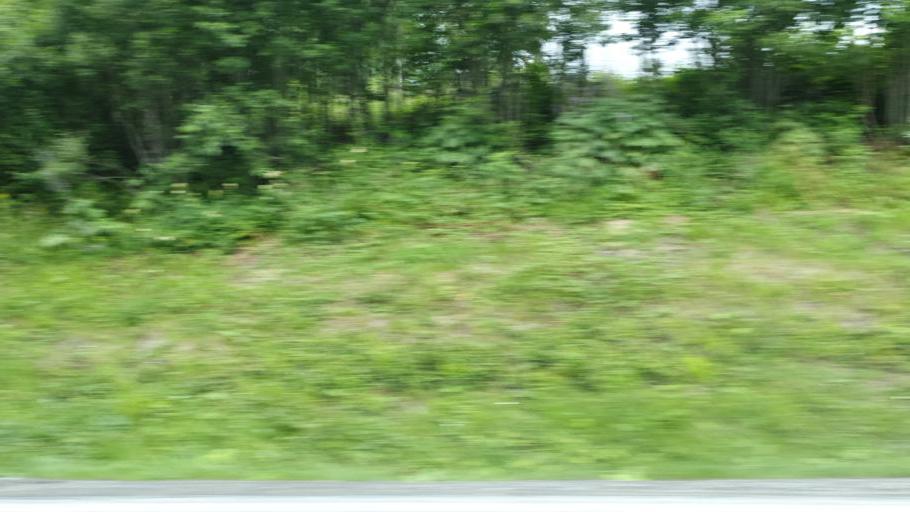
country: NO
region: Sor-Trondelag
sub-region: Rennebu
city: Berkak
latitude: 62.8801
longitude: 10.0913
